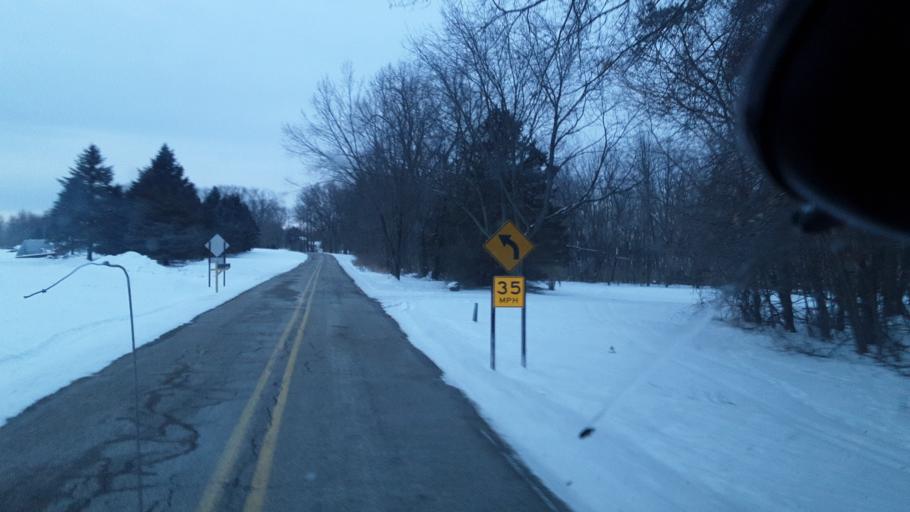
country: US
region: Michigan
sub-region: Ingham County
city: Leslie
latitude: 42.4451
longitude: -84.3451
